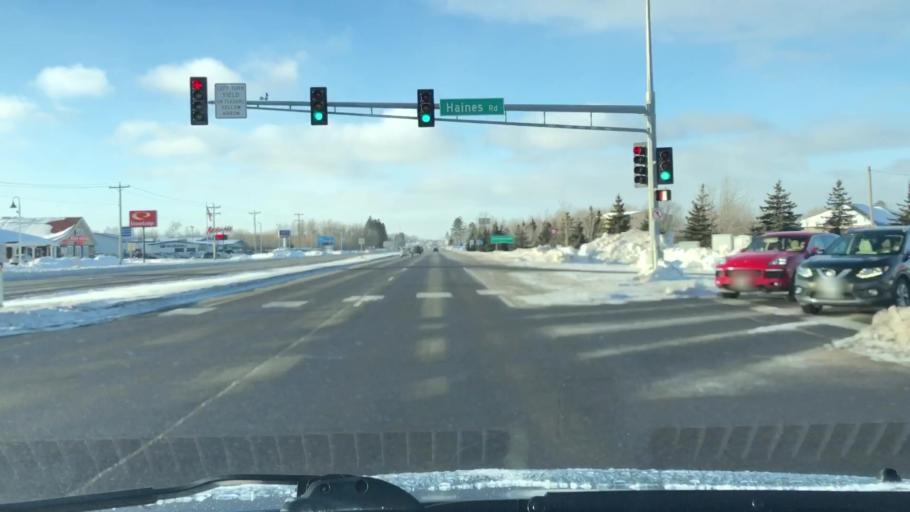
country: US
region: Minnesota
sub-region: Saint Louis County
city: Hermantown
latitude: 46.8149
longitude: -92.1748
